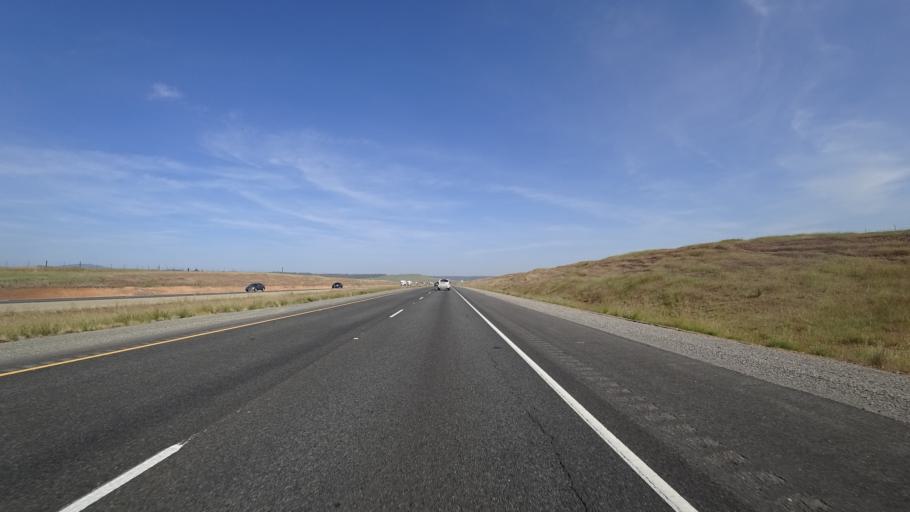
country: US
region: California
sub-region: Butte County
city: Thermalito
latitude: 39.5990
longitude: -121.6574
